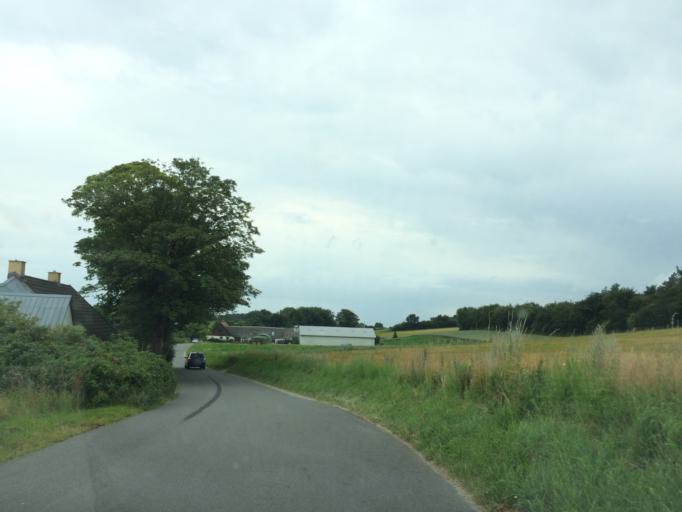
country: DK
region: Central Jutland
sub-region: Syddjurs Kommune
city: Ronde
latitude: 56.2356
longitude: 10.5246
